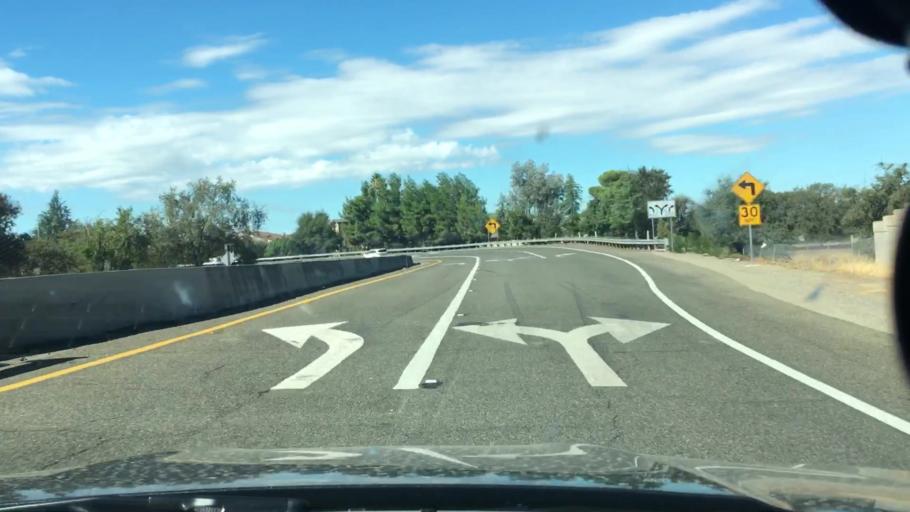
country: US
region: California
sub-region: Sacramento County
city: Foothill Farms
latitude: 38.6622
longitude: -121.3603
